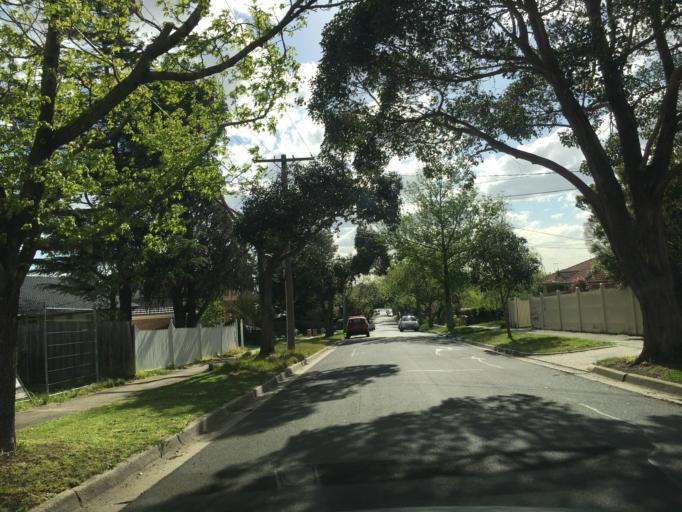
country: AU
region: Victoria
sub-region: Monash
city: Notting Hill
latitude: -37.8911
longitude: 145.1675
